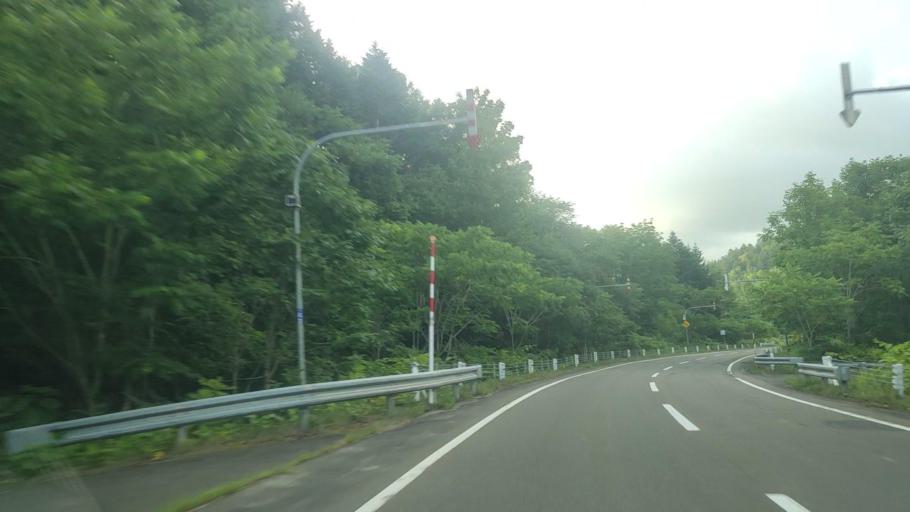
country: JP
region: Hokkaido
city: Bibai
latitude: 43.1259
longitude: 142.1016
